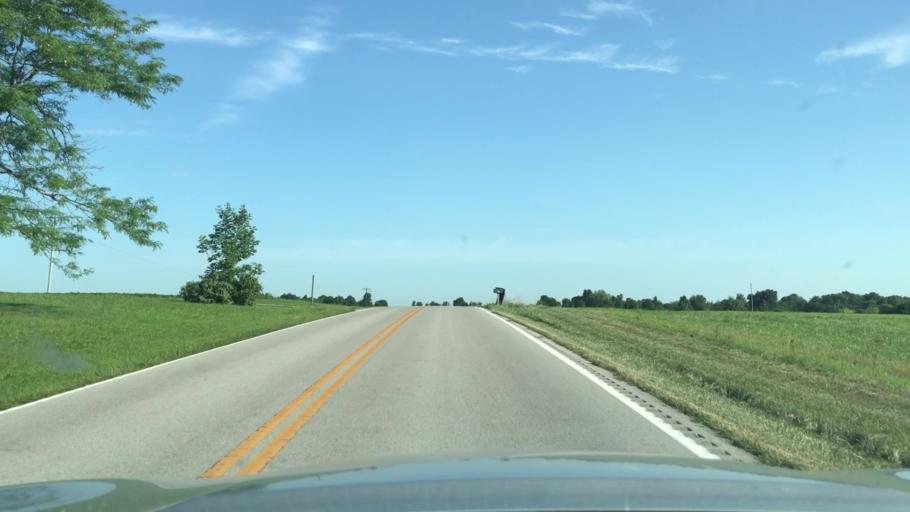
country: US
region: Kentucky
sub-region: Muhlenberg County
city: Greenville
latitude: 37.0158
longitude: -87.1315
